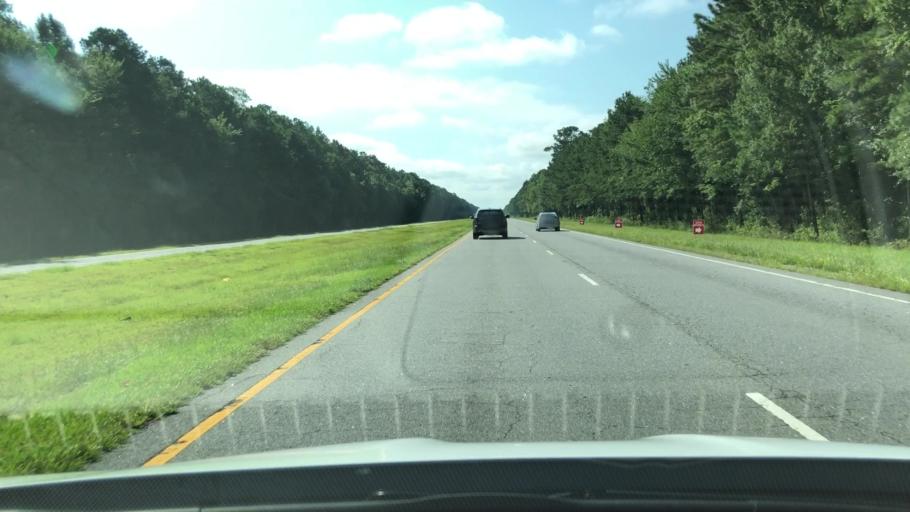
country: US
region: North Carolina
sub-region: Pasquotank County
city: Elizabeth City
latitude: 36.4009
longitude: -76.3326
